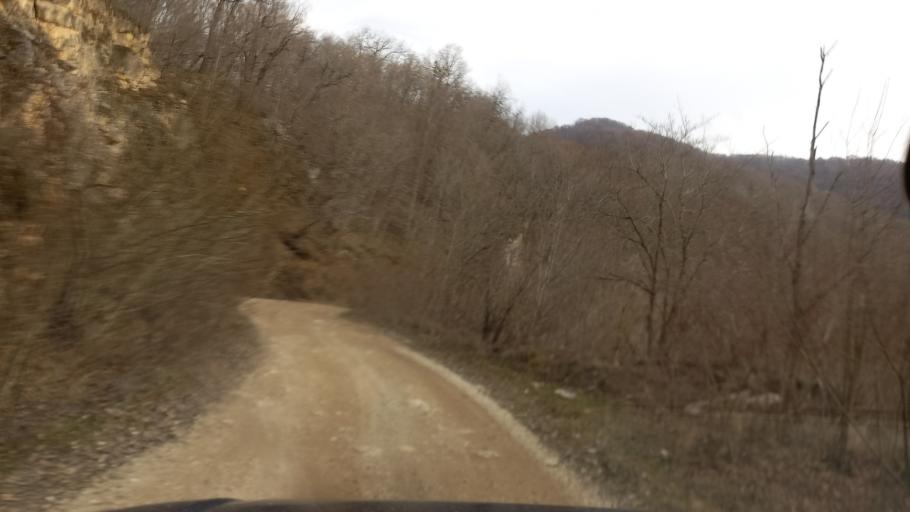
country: RU
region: Adygeya
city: Kamennomostskiy
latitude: 44.1581
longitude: 40.3002
